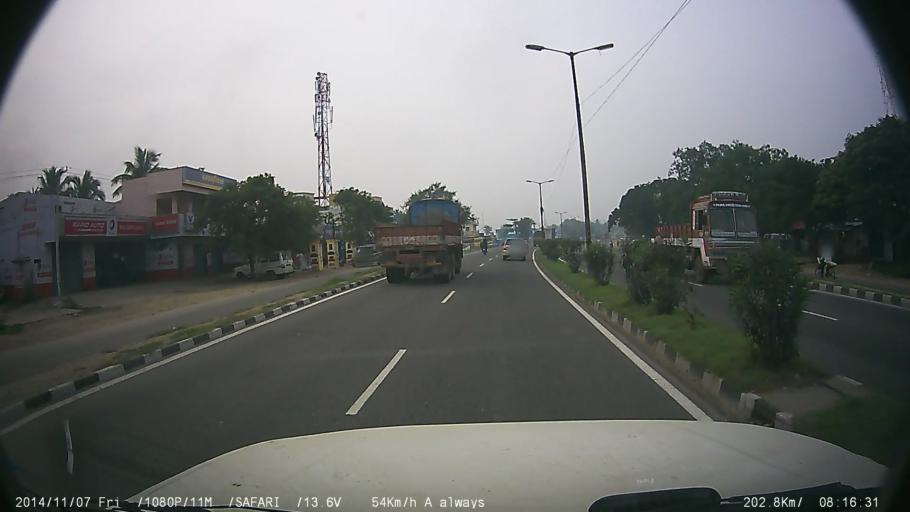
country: IN
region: Tamil Nadu
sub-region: Salem
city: Salem
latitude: 11.6740
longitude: 78.1279
